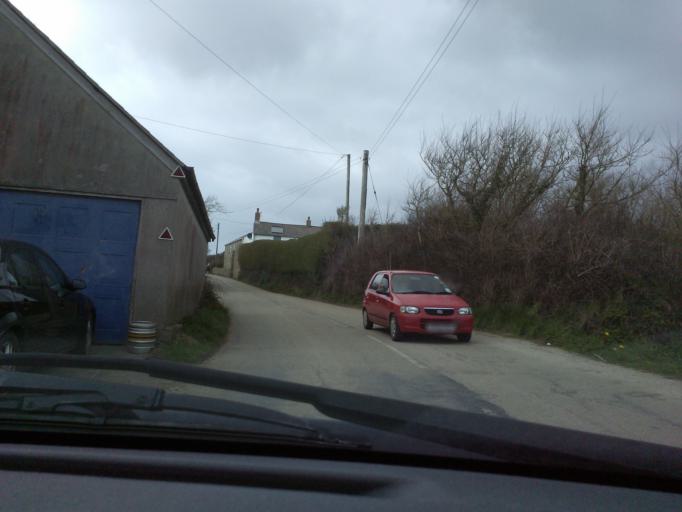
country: GB
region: England
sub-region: Cornwall
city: Sennen
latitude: 50.0573
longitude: -5.6667
